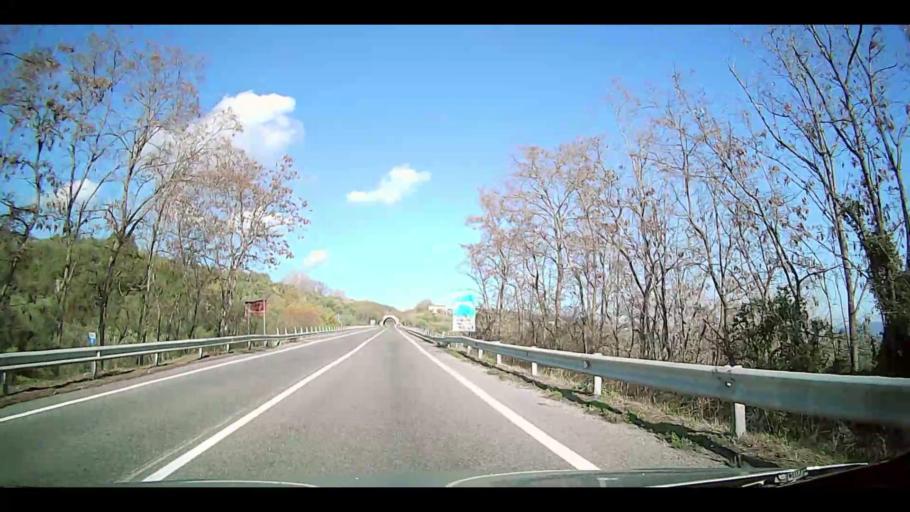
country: IT
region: Calabria
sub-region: Provincia di Crotone
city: Caccuri
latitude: 39.2158
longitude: 16.7972
